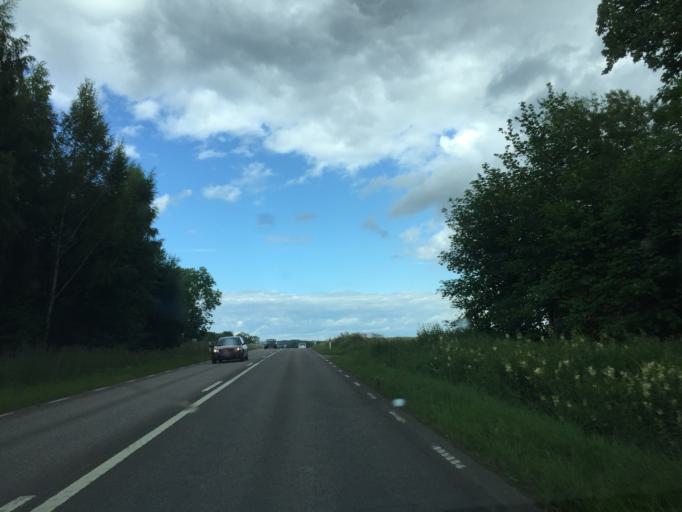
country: SE
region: OEstergoetland
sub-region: Motala Kommun
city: Motala
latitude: 58.4877
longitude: 14.9923
